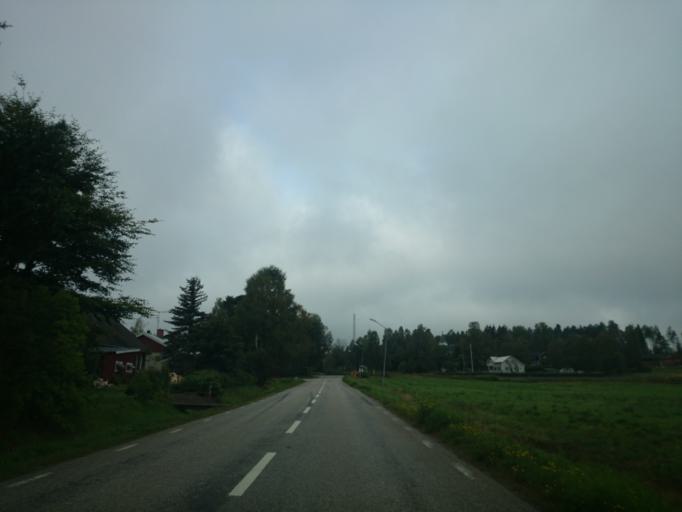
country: SE
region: Gaevleborg
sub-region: Nordanstigs Kommun
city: Bergsjoe
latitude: 61.9765
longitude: 17.2510
